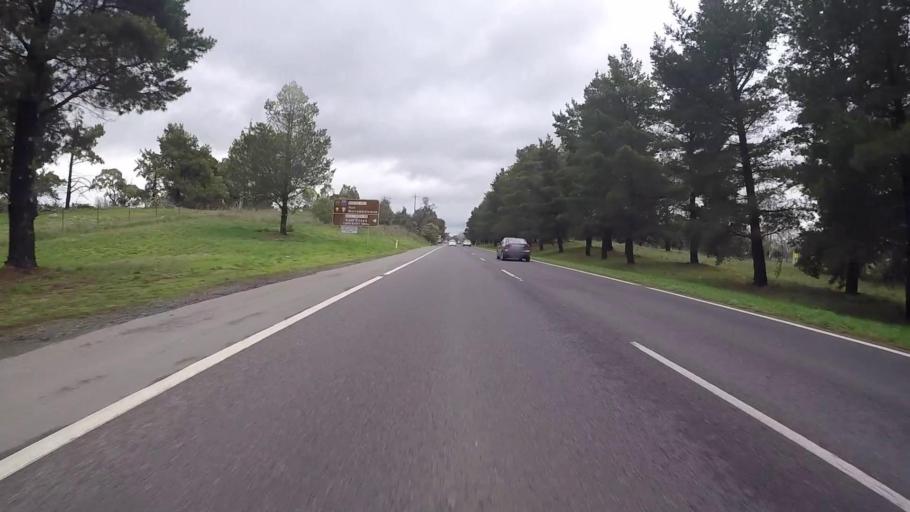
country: AU
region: Australian Capital Territory
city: Belconnen
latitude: -35.1980
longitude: 149.0900
